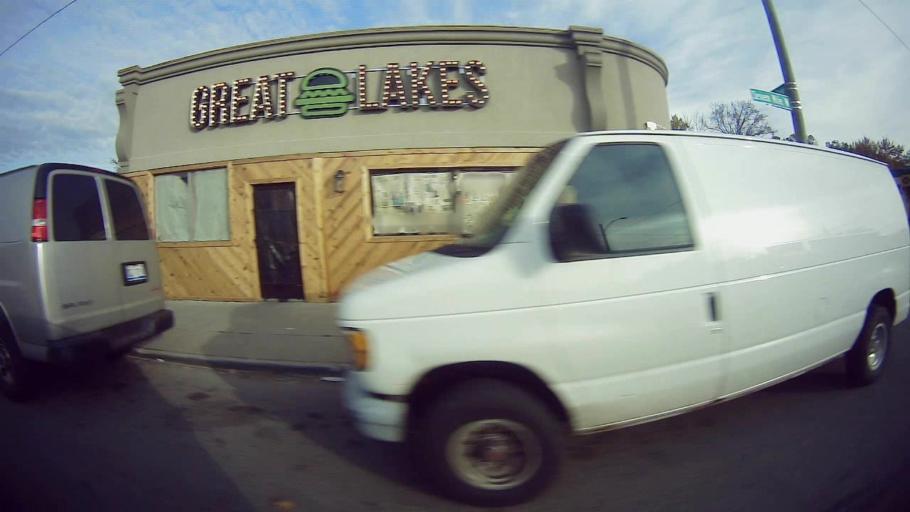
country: US
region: Michigan
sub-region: Oakland County
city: Southfield
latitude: 42.4301
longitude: -83.2163
